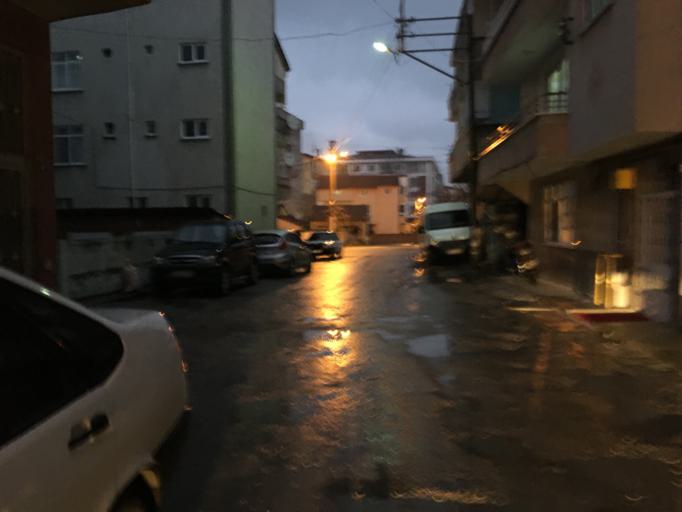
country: TR
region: Samsun
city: Alacam
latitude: 41.6122
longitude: 35.6053
